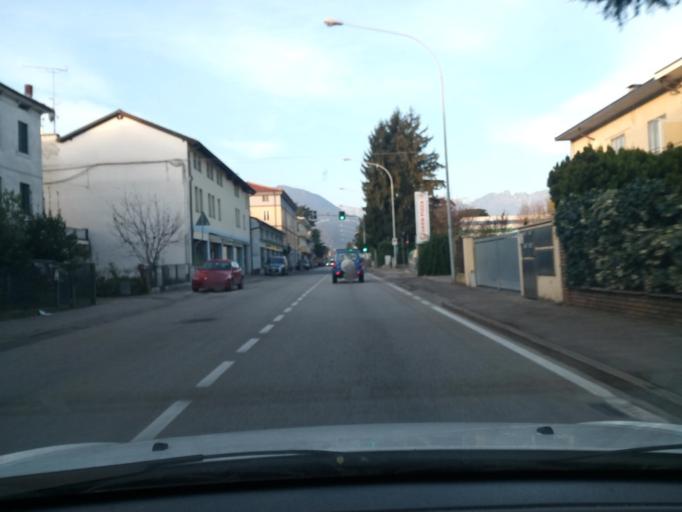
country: IT
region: Veneto
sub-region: Provincia di Vicenza
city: Schio
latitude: 45.7159
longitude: 11.3454
